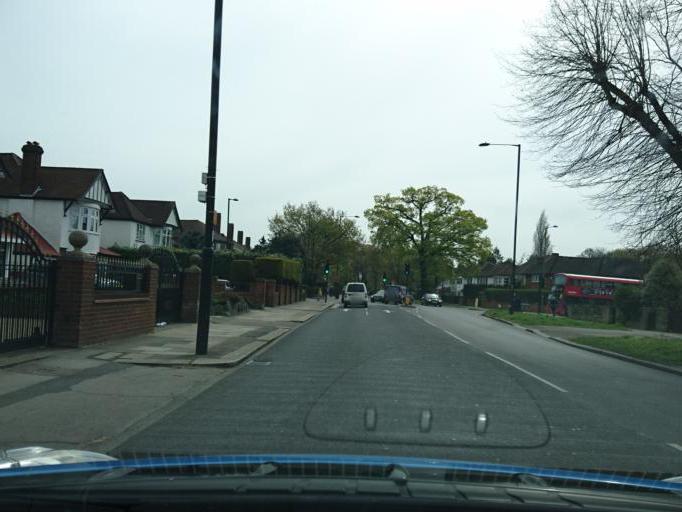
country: GB
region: England
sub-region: Greater London
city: Hadley Wood
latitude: 51.6370
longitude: -0.1389
